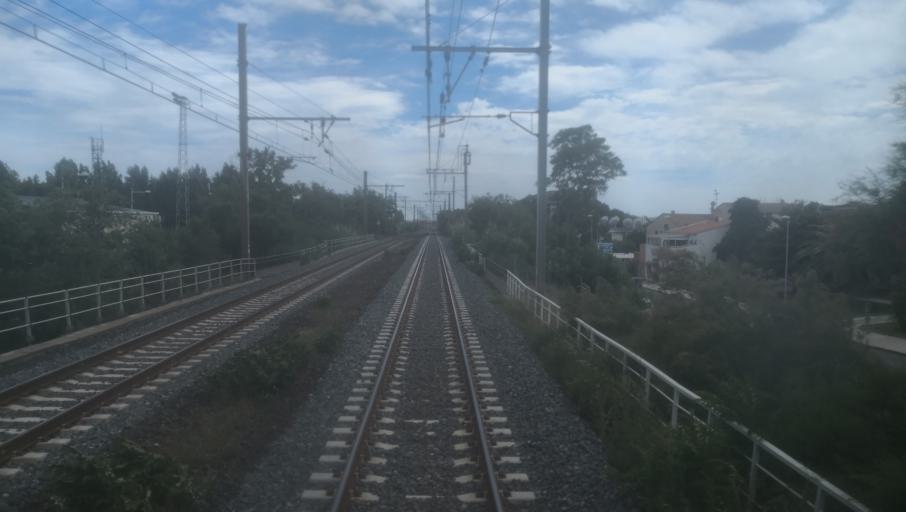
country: FR
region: Languedoc-Roussillon
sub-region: Departement de l'Herault
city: Frontignan
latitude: 43.4437
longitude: 3.7587
